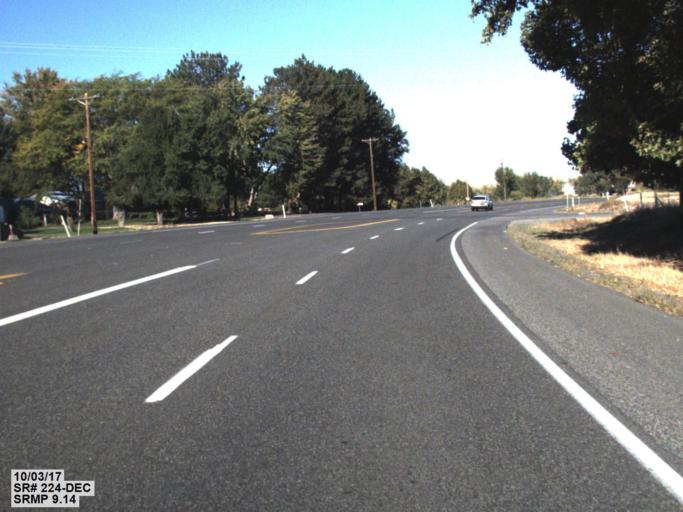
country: US
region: Washington
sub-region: Benton County
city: Richland
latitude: 46.2936
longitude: -119.3209
